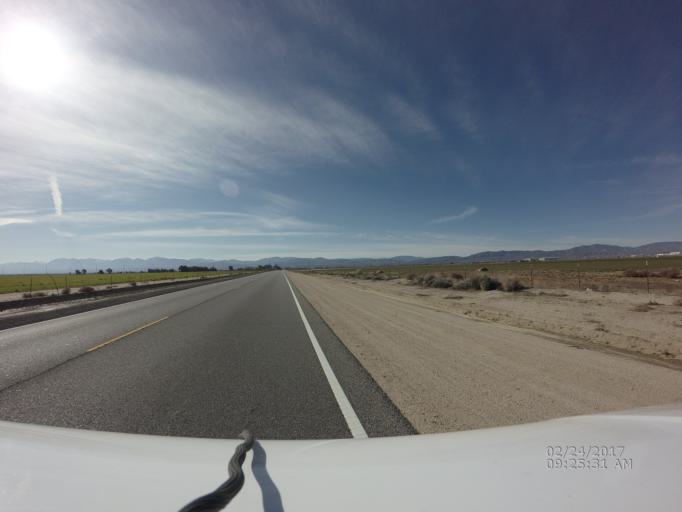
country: US
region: California
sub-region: Los Angeles County
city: Palmdale
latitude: 34.6367
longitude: -118.0409
